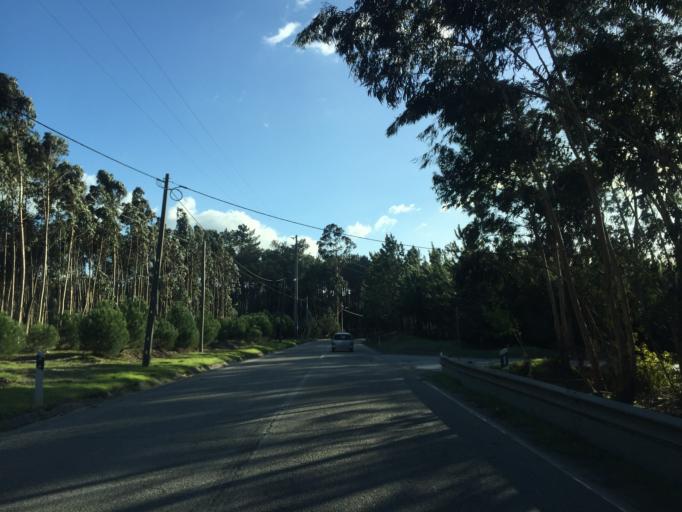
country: PT
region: Leiria
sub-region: Leiria
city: Monte Redondo
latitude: 39.9187
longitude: -8.8123
